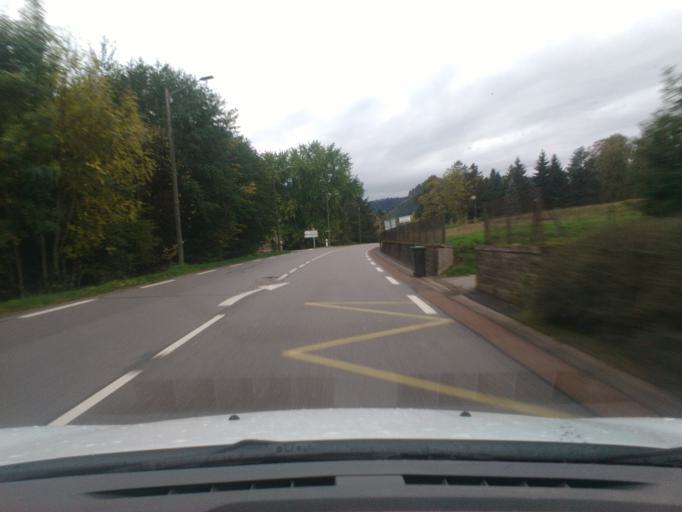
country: FR
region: Lorraine
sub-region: Departement des Vosges
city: Taintrux
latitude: 48.2749
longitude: 6.9000
